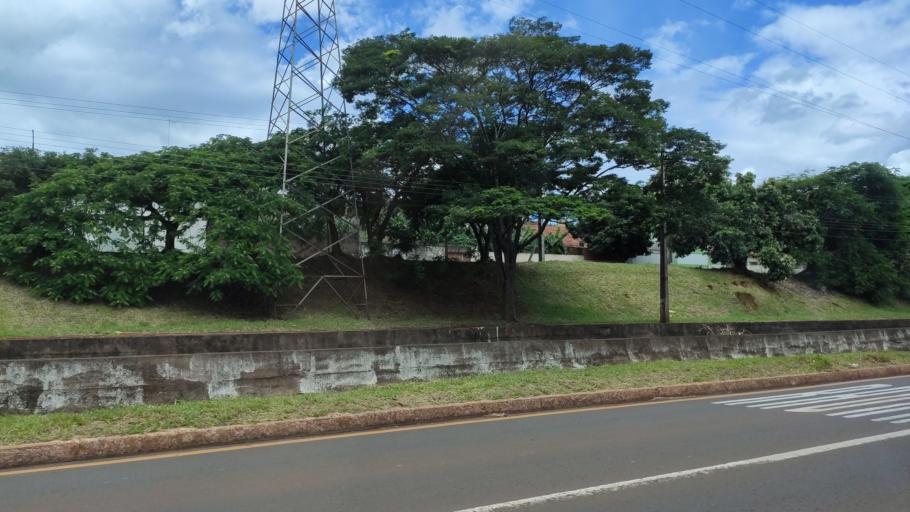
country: BR
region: Parana
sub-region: Londrina
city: Londrina
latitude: -23.3306
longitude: -51.1460
